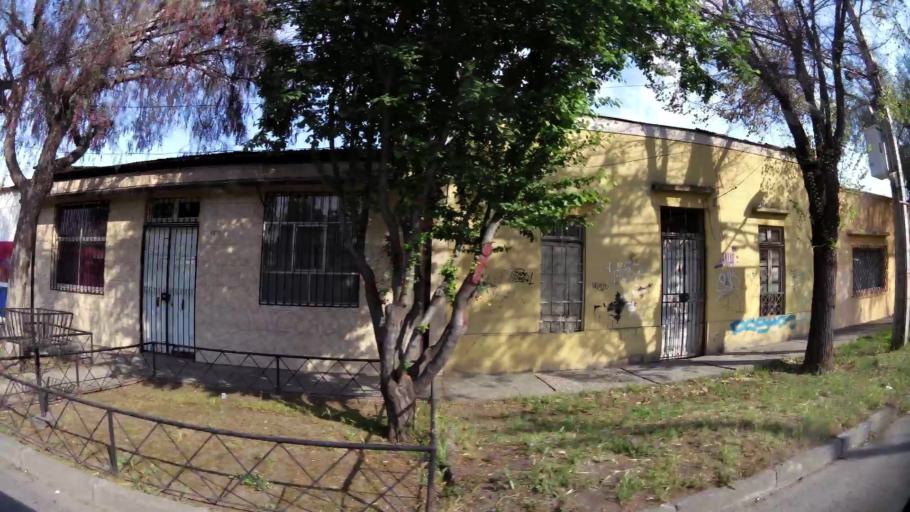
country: CL
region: Santiago Metropolitan
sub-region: Provincia de Maipo
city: San Bernardo
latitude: -33.5952
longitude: -70.7092
